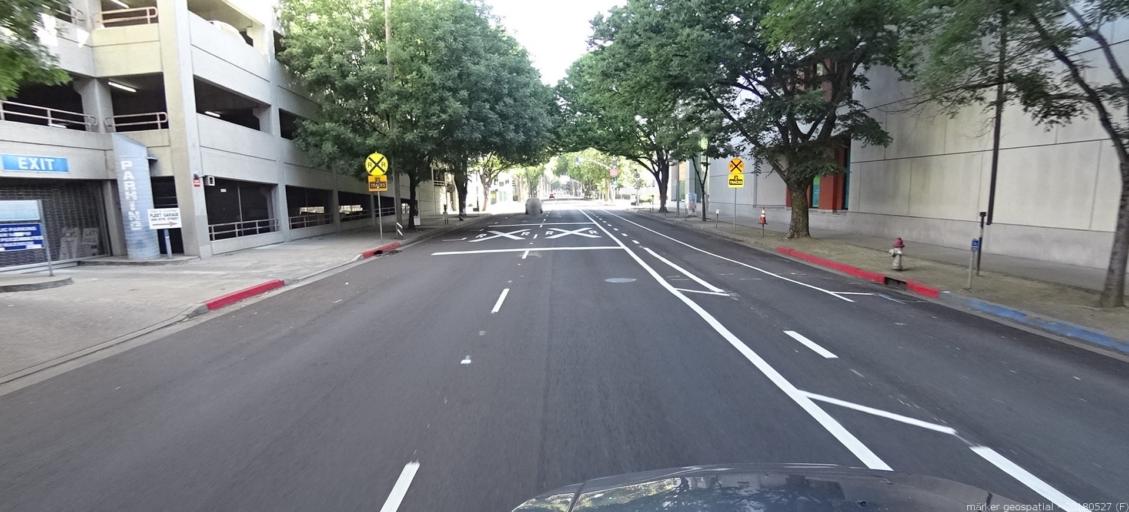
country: US
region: California
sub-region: Sacramento County
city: Sacramento
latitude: 38.5741
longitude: -121.4962
